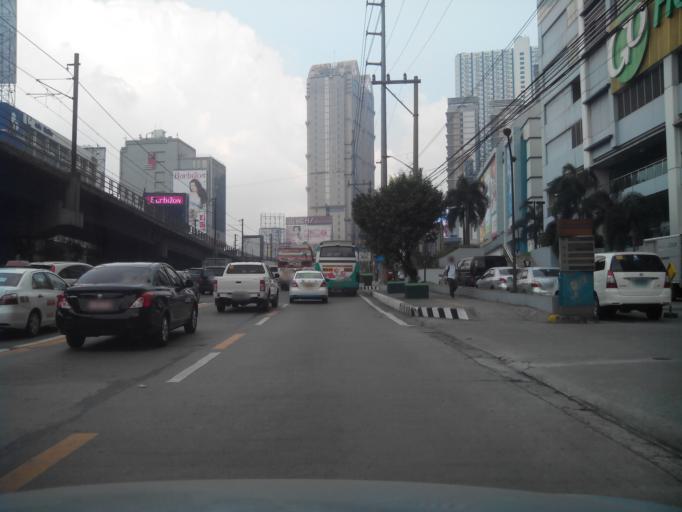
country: PH
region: Metro Manila
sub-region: Mandaluyong
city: Mandaluyong City
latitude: 14.5698
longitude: 121.0466
